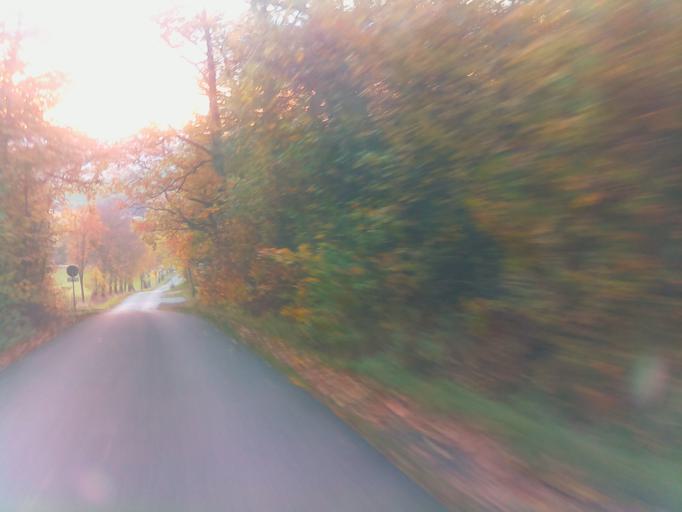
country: DE
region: Thuringia
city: Urnshausen
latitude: 50.7411
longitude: 10.1910
